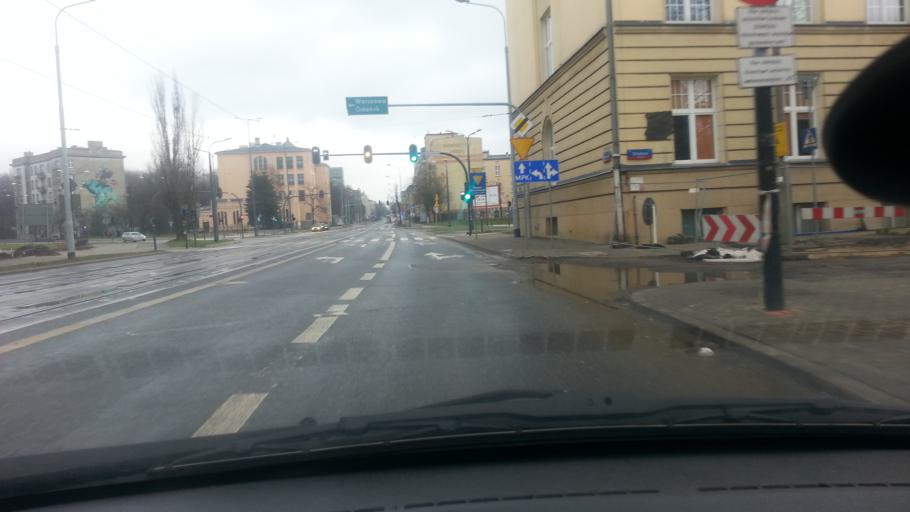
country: PL
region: Lodz Voivodeship
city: Lodz
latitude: 51.7720
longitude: 19.4716
